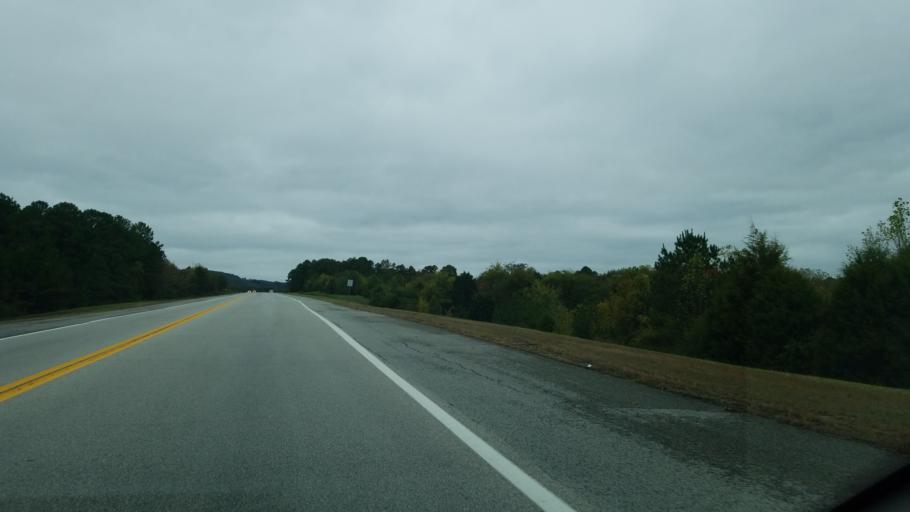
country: US
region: Tennessee
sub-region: Rhea County
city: Dayton
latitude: 35.4611
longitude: -85.0146
